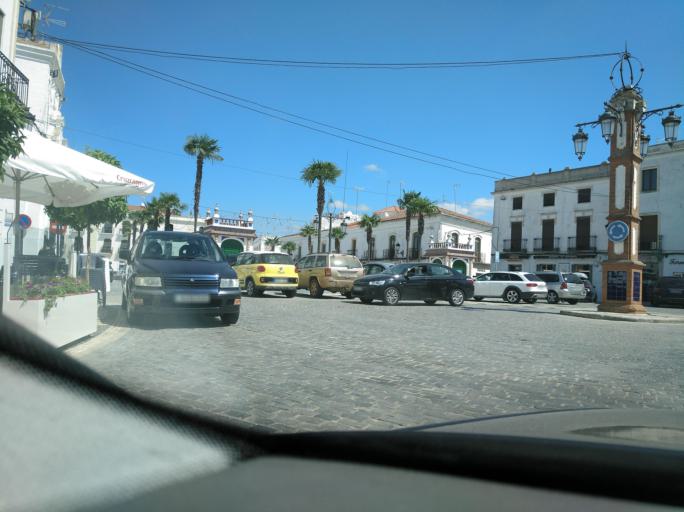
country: ES
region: Extremadura
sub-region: Provincia de Badajoz
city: Olivenza
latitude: 38.6839
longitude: -7.1023
